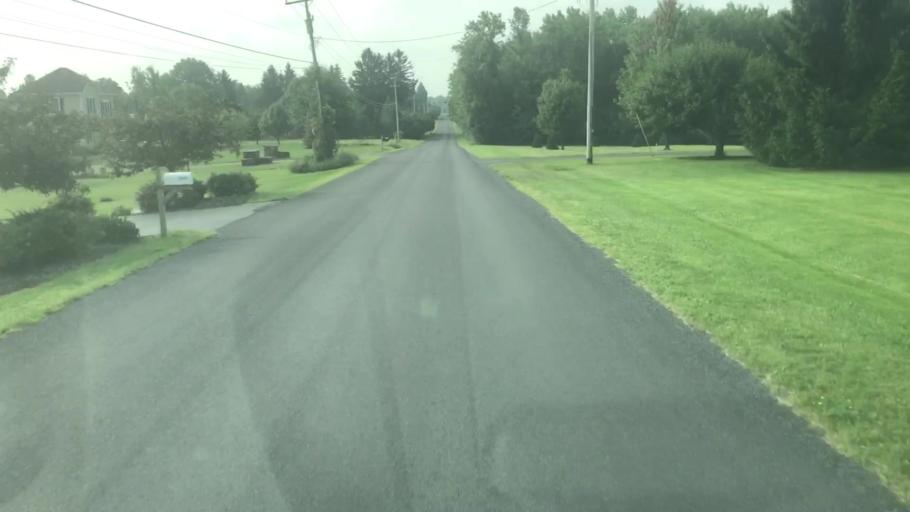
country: US
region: New York
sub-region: Onondaga County
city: Skaneateles
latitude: 42.9231
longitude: -76.4569
